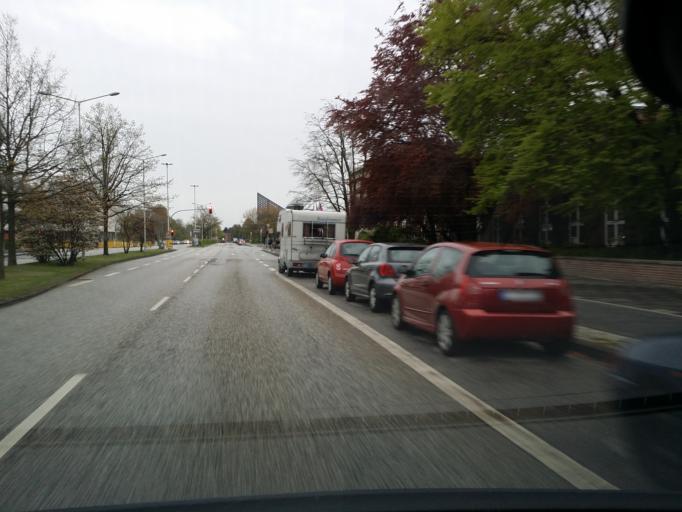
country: DE
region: Schleswig-Holstein
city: Kiel
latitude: 54.3397
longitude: 10.1256
